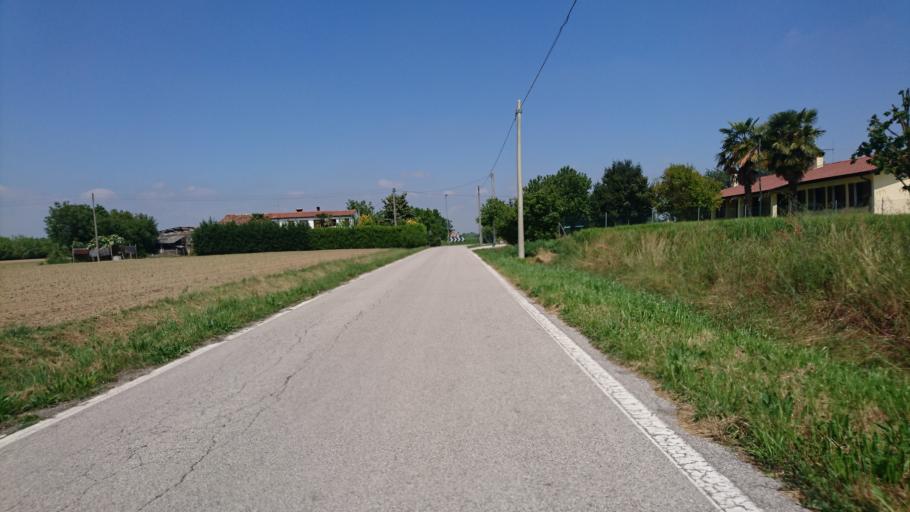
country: IT
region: Veneto
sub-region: Provincia di Padova
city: Bertipaglia
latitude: 45.3240
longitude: 11.8905
